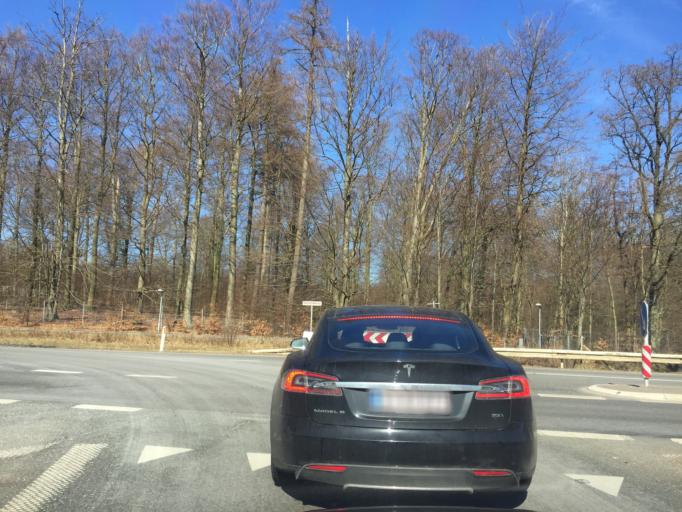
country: DK
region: Capital Region
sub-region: Fredensborg Kommune
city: Humlebaek
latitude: 55.9847
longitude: 12.5154
